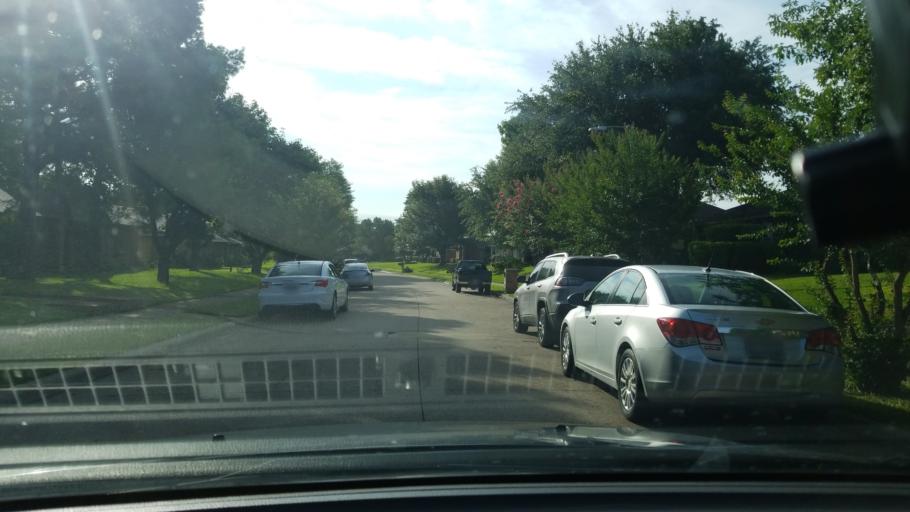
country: US
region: Texas
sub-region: Dallas County
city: Mesquite
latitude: 32.8090
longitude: -96.6070
